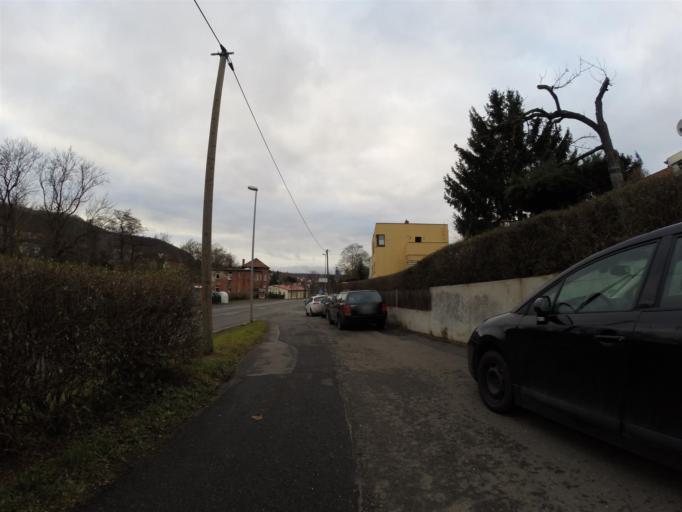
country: DE
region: Thuringia
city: Jena
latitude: 50.9340
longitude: 11.6264
